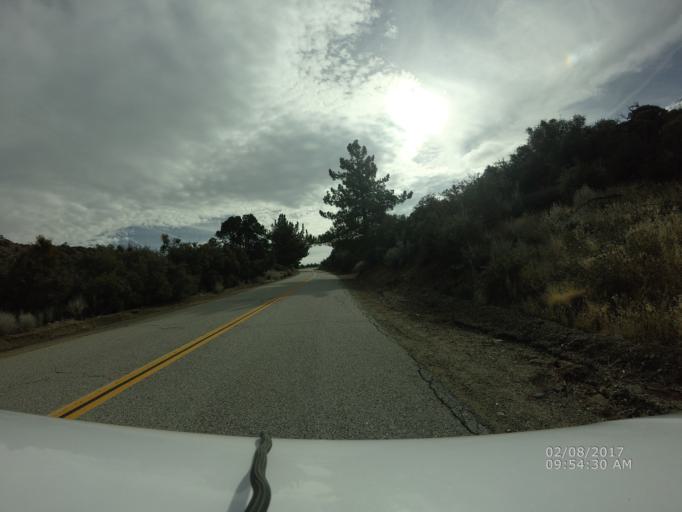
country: US
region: California
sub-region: San Bernardino County
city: Pinon Hills
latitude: 34.4208
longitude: -117.7956
